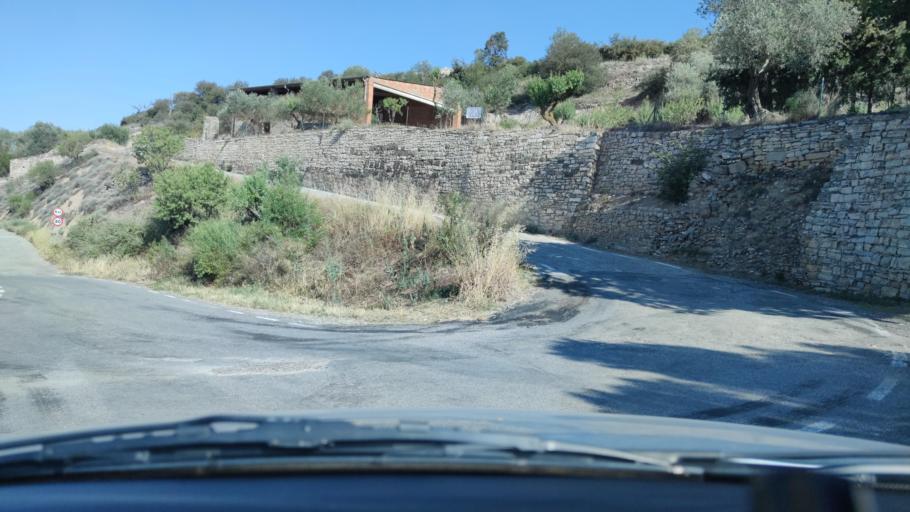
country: ES
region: Catalonia
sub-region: Provincia de Lleida
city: Ivorra
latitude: 41.7381
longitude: 1.3484
